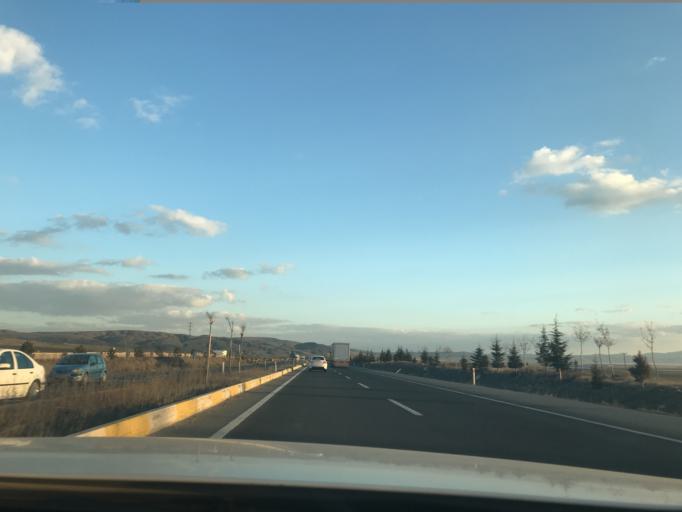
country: TR
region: Ankara
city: Altpinar
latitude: 39.3805
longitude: 32.8939
